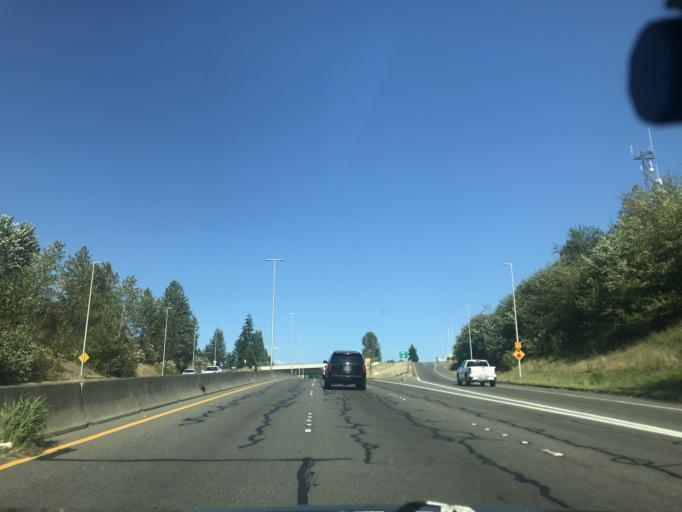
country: US
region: Washington
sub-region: King County
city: Lea Hill
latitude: 47.3557
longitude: -122.2004
